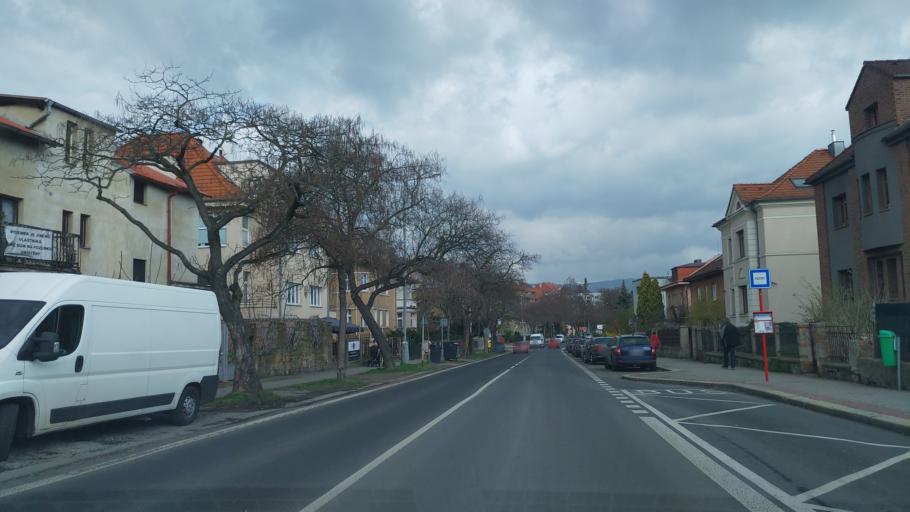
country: CZ
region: Ustecky
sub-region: Okres Usti nad Labem
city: Usti nad Labem
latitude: 50.6691
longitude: 14.0171
